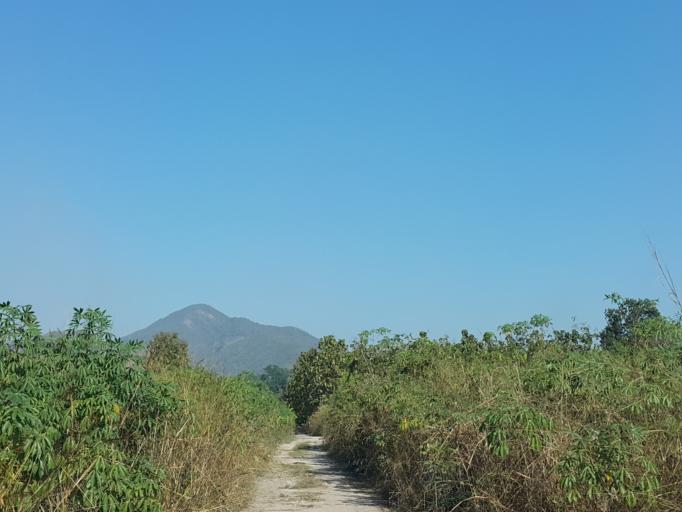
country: TH
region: Sukhothai
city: Thung Saliam
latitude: 17.3234
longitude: 99.4624
